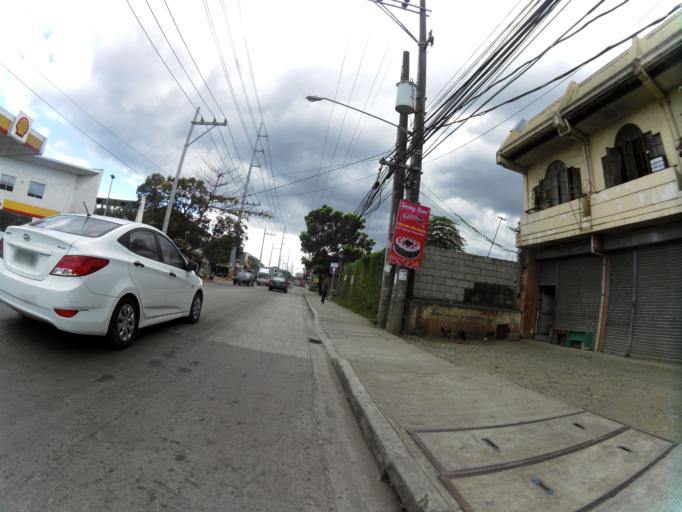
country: PH
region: Calabarzon
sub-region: Province of Rizal
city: Antipolo
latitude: 14.6336
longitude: 121.1215
